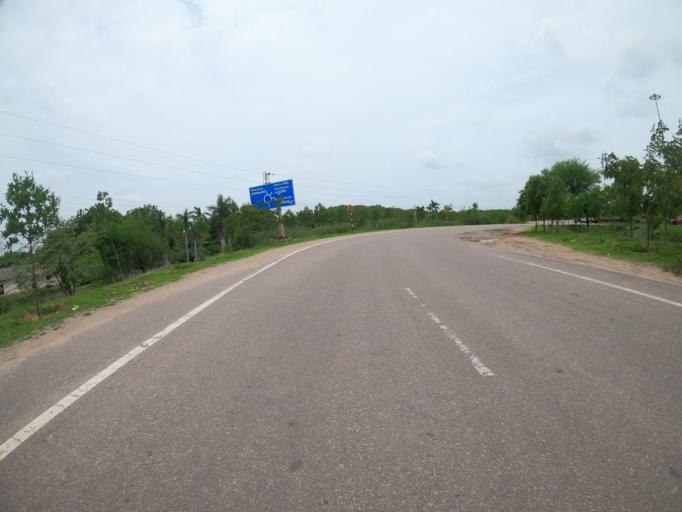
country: IN
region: Telangana
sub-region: Hyderabad
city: Hyderabad
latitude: 17.3481
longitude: 78.3589
